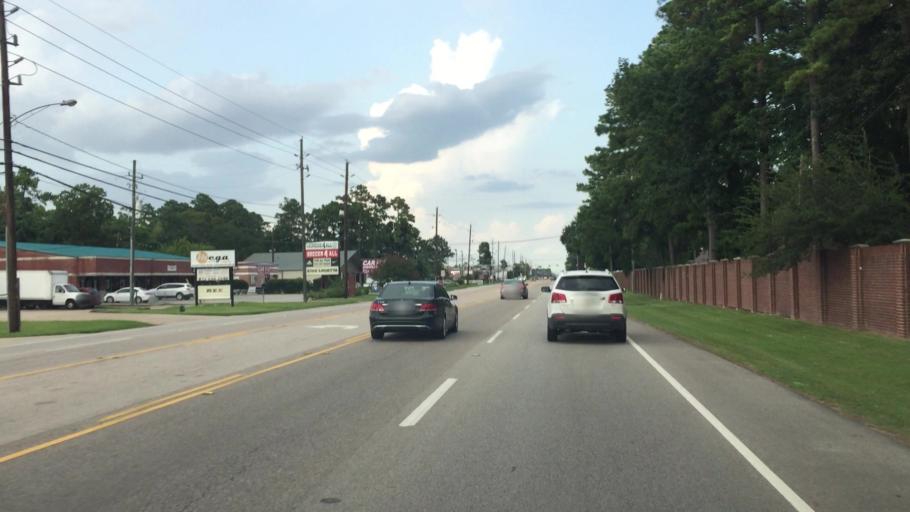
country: US
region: Texas
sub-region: Harris County
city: Spring
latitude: 30.0250
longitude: -95.5165
